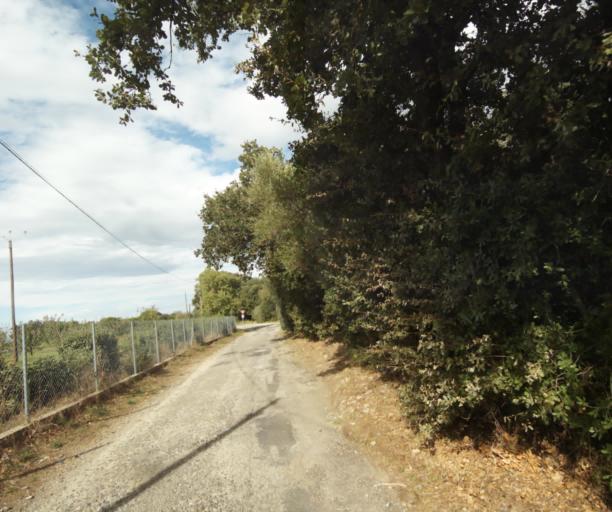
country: FR
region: Languedoc-Roussillon
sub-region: Departement des Pyrenees-Orientales
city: Sant Andreu de Sureda
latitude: 42.5308
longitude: 2.9862
